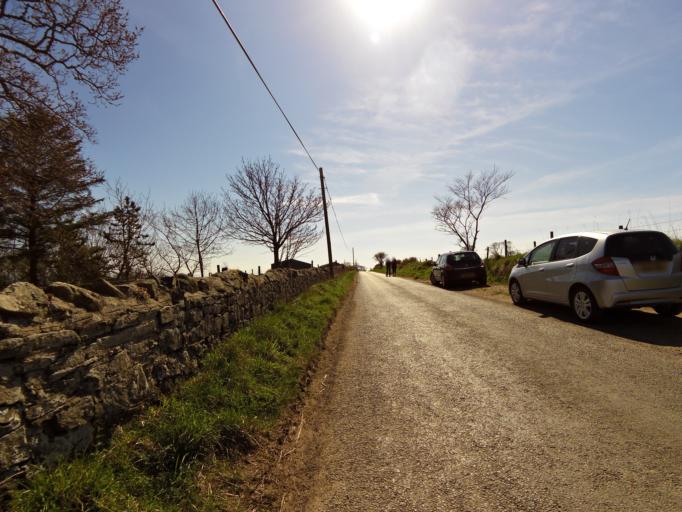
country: GB
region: Scotland
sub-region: Angus
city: Montrose
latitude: 56.6861
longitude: -2.4579
